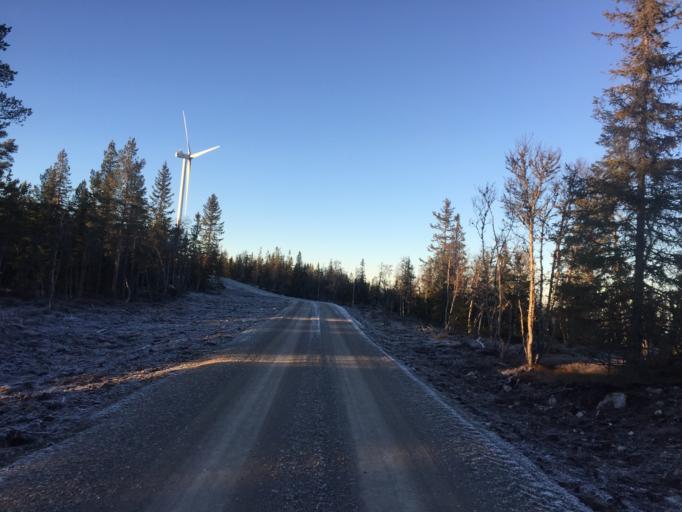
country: NO
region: Hedmark
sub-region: Elverum
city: Elverum
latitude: 61.2103
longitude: 11.7858
